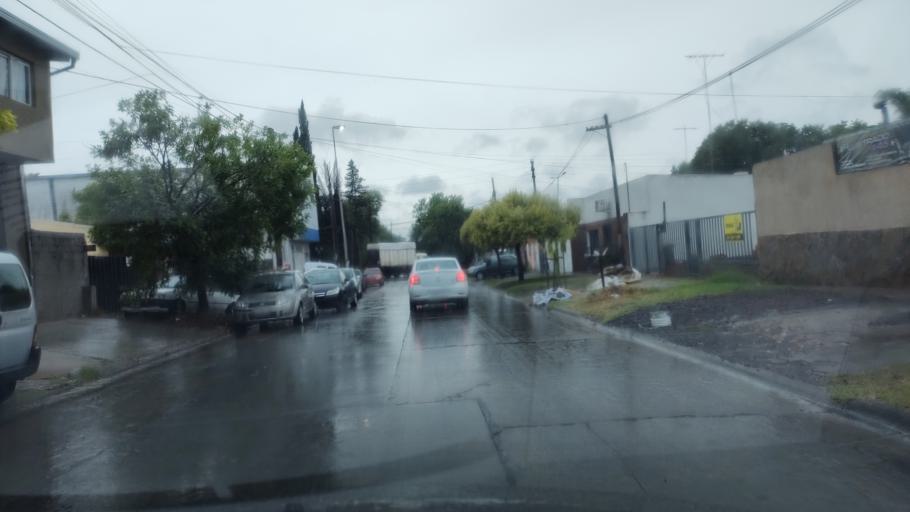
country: AR
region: Buenos Aires
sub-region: Partido de La Plata
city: La Plata
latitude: -34.9462
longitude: -57.9921
